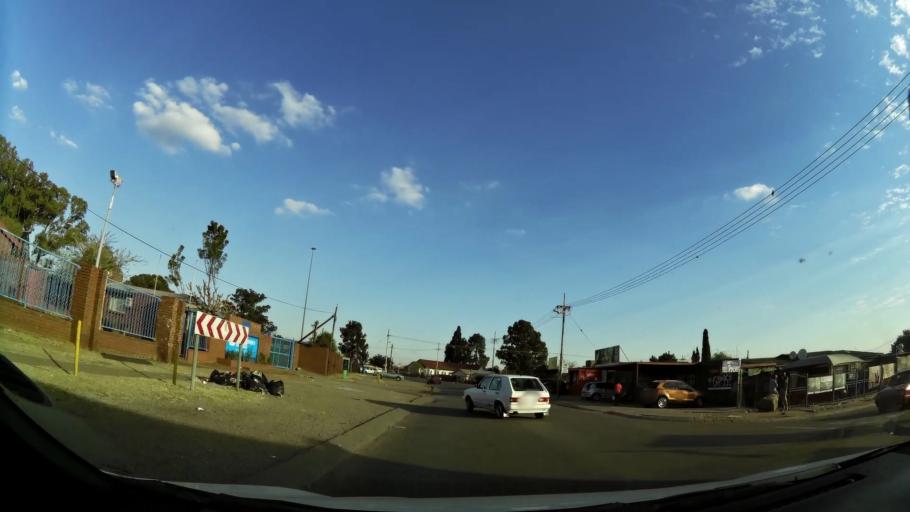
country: ZA
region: Gauteng
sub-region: City of Tshwane Metropolitan Municipality
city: Cullinan
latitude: -25.7118
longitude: 28.3738
